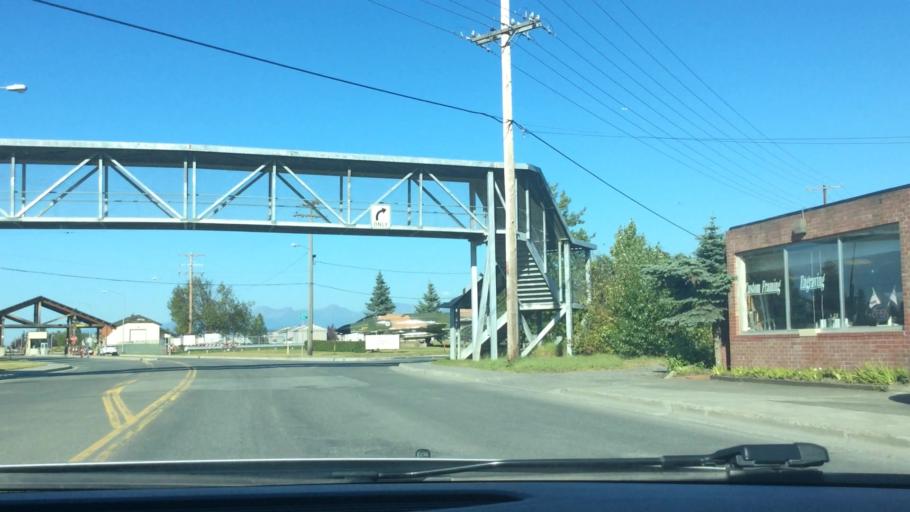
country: US
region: Alaska
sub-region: Anchorage Municipality
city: Anchorage
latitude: 61.2310
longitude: -149.8729
